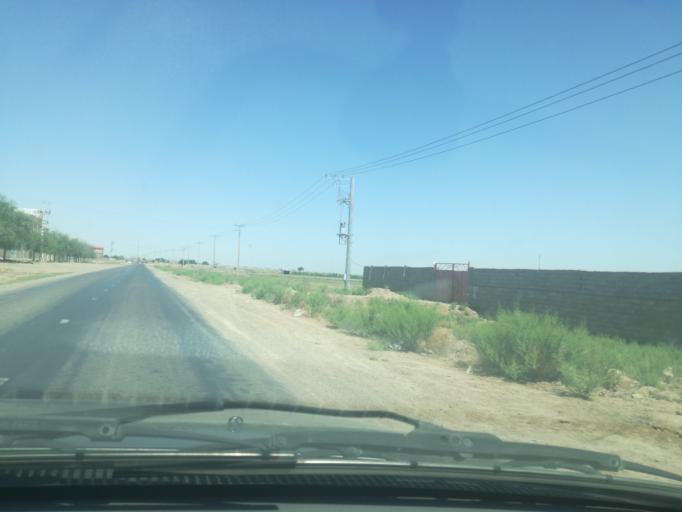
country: IR
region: Razavi Khorasan
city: Sarakhs
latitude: 36.5646
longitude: 61.1440
